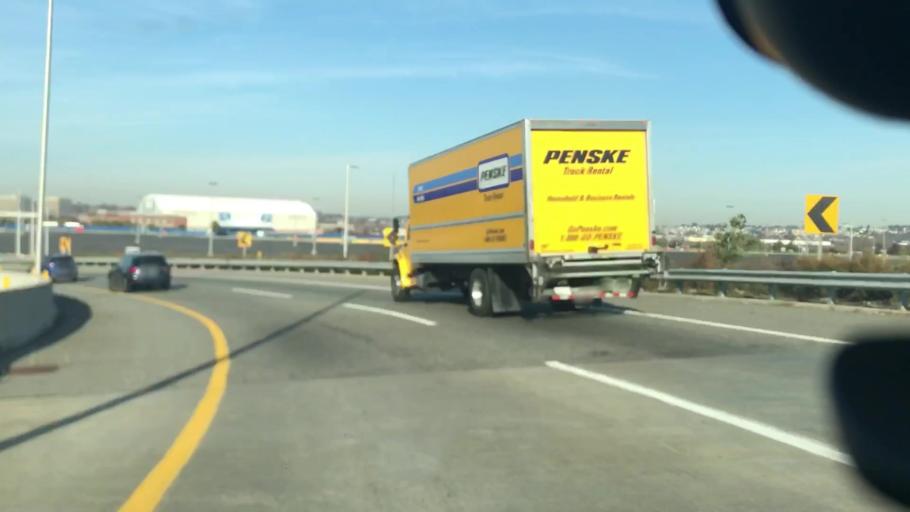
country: US
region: New Jersey
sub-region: Bergen County
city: East Rutherford
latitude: 40.8101
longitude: -74.0791
